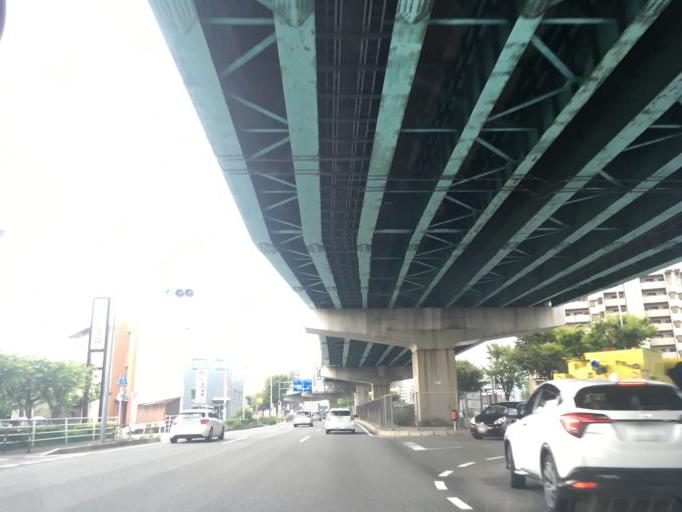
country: JP
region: Fukuoka
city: Fukuoka-shi
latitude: 33.5883
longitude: 130.4386
